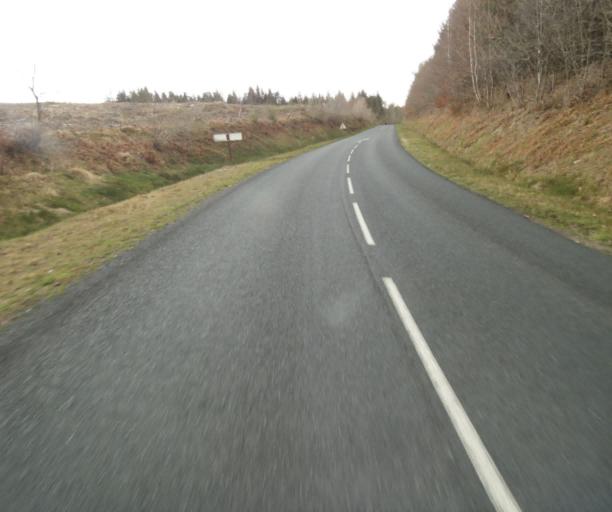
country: FR
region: Limousin
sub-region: Departement de la Correze
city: Egletons
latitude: 45.2759
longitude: 1.9921
